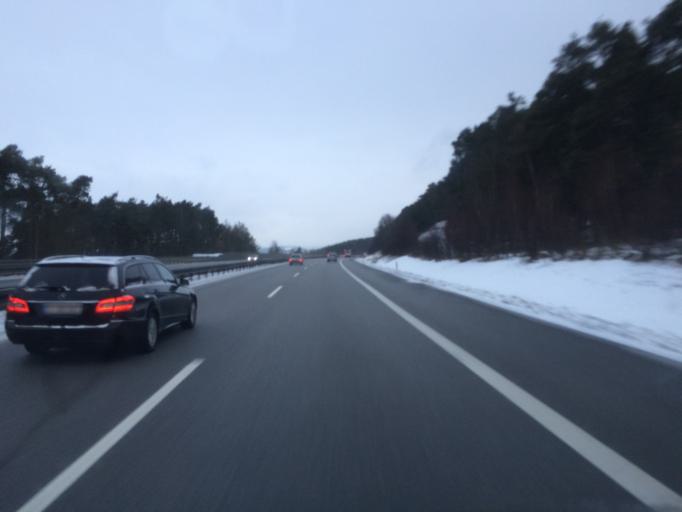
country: DE
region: Bavaria
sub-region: Upper Palatinate
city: Maxhutte-Haidhof
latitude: 49.1965
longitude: 12.1168
